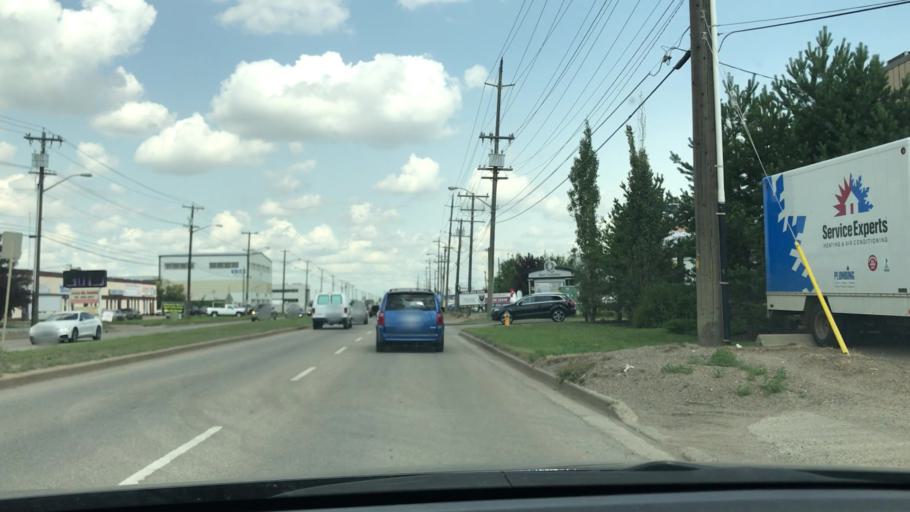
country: CA
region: Alberta
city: Edmonton
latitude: 53.5086
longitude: -113.4182
